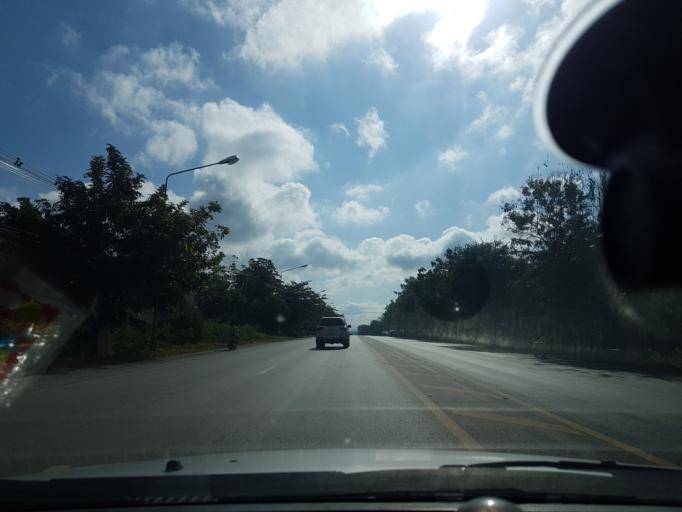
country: TH
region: Lop Buri
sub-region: Amphoe Tha Luang
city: Tha Luang
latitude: 15.0788
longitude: 101.0508
